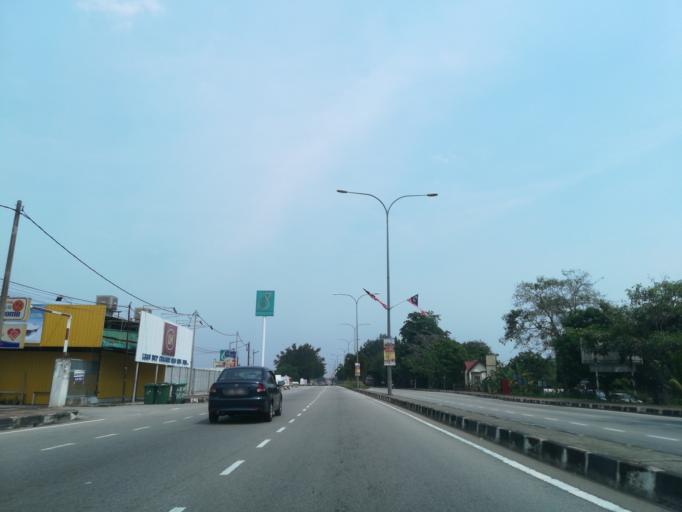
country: MY
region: Kedah
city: Kulim
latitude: 5.4092
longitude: 100.5486
